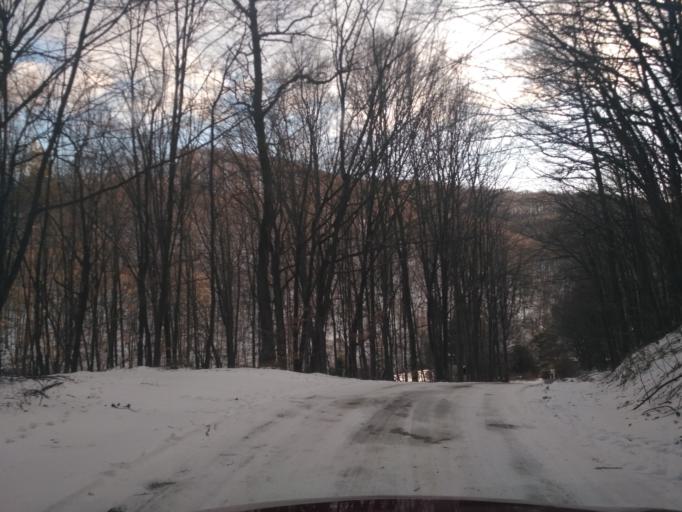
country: SK
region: Kosicky
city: Kosice
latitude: 48.7251
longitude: 21.1625
